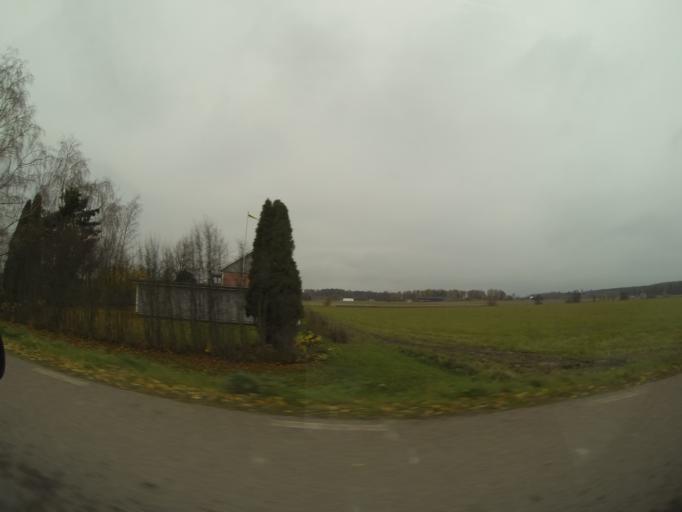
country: SE
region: Vaestmanland
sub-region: Kopings Kommun
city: Koping
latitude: 59.5755
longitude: 16.0832
